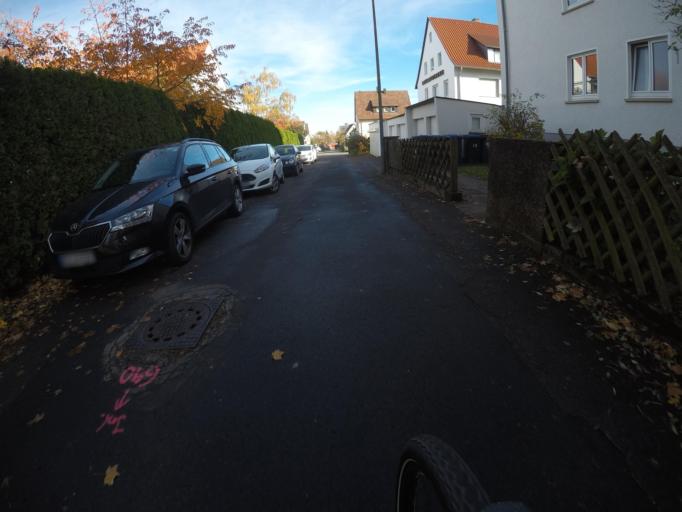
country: DE
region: Baden-Wuerttemberg
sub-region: Regierungsbezirk Stuttgart
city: Leinfelden-Echterdingen
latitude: 48.6962
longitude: 9.1401
